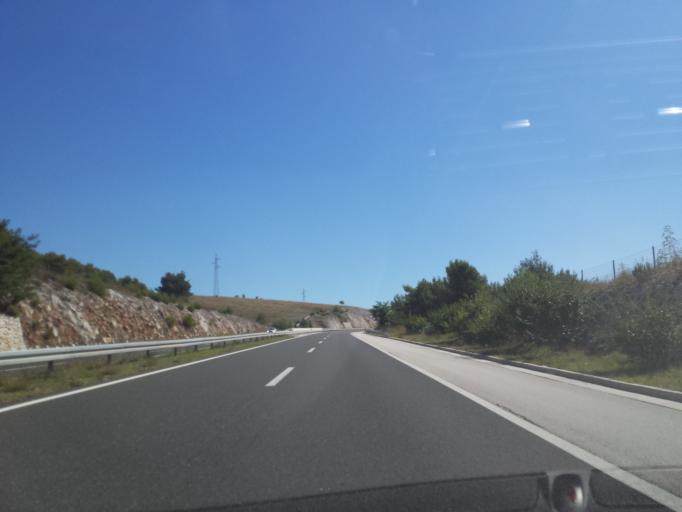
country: HR
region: Splitsko-Dalmatinska
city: Dugopolje
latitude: 43.6029
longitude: 16.6127
